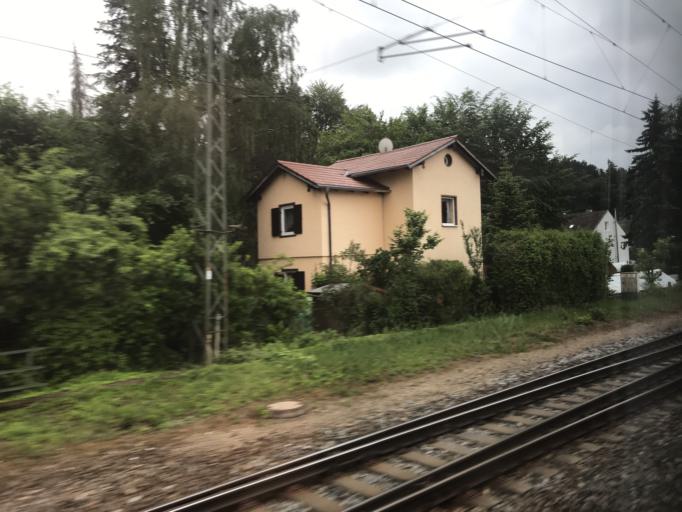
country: DE
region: Bavaria
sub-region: Swabia
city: Stadtbergen
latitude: 48.3842
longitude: 10.8158
